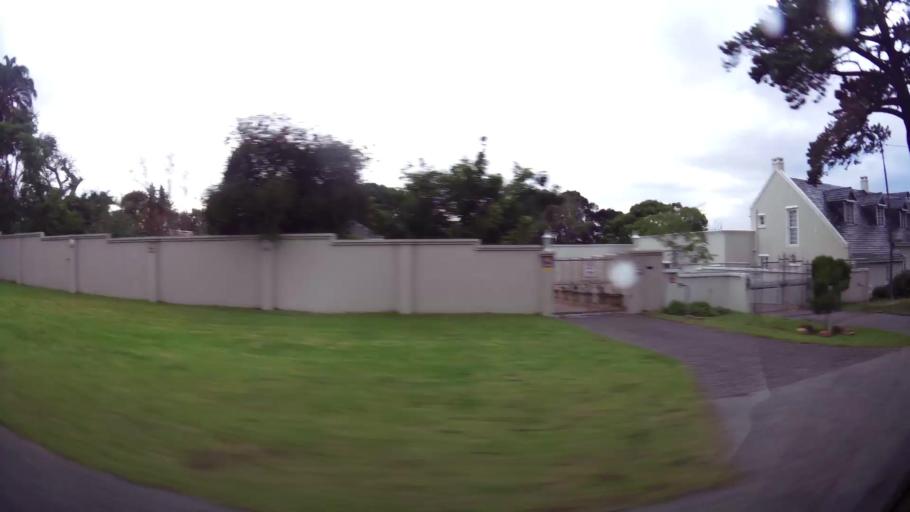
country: ZA
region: Eastern Cape
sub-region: Nelson Mandela Bay Metropolitan Municipality
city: Port Elizabeth
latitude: -33.9760
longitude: 25.5811
